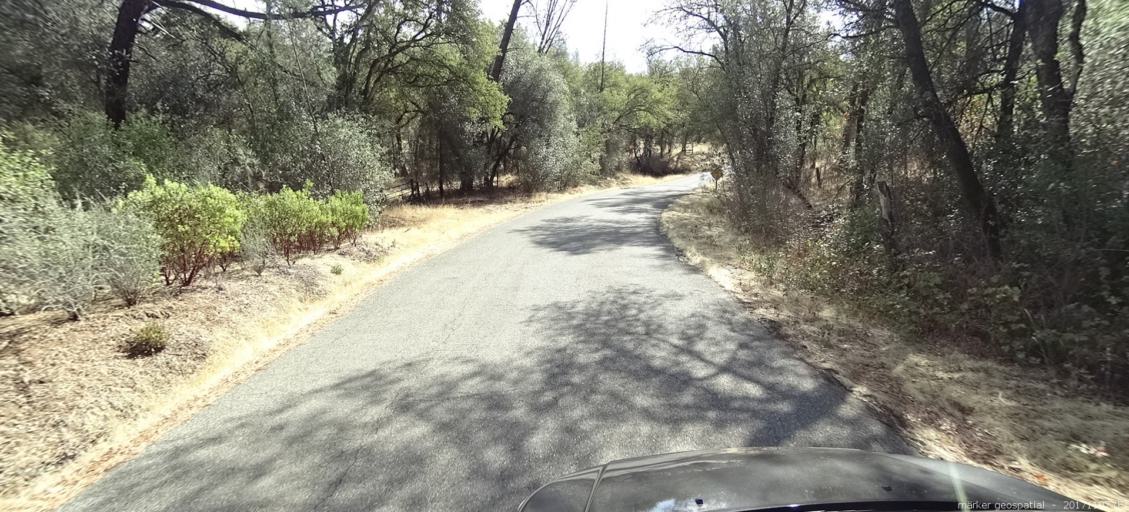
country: US
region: California
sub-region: Shasta County
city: Shasta
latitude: 40.5203
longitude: -122.5507
